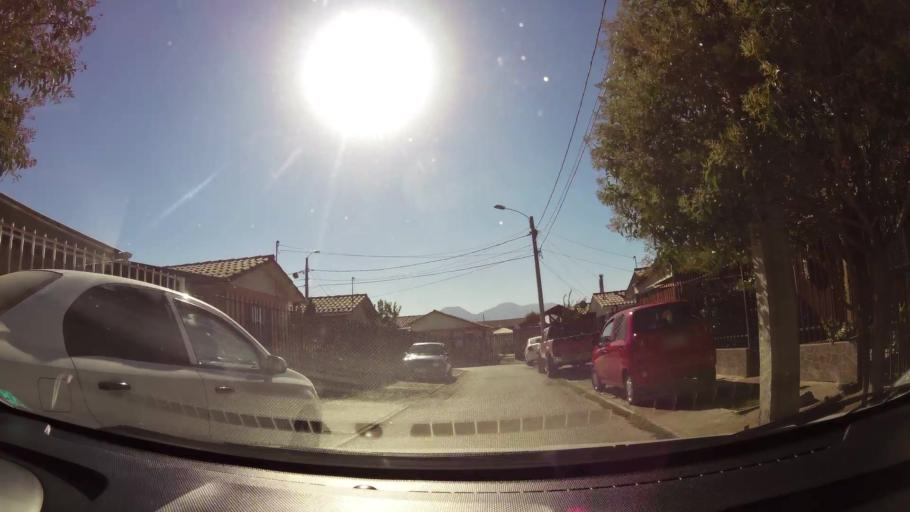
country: CL
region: O'Higgins
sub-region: Provincia de Cachapoal
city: Rancagua
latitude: -34.1829
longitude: -70.7682
